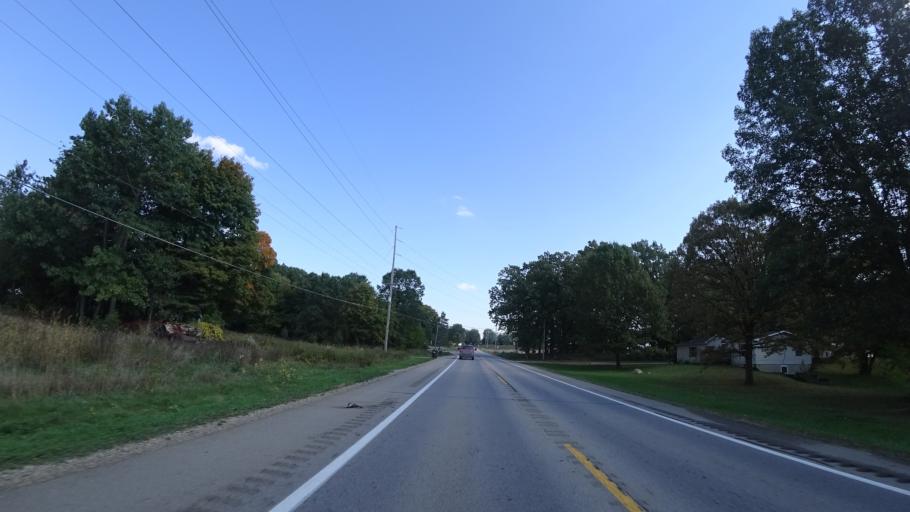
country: US
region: Michigan
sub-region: Jackson County
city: Concord
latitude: 42.1643
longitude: -84.6846
